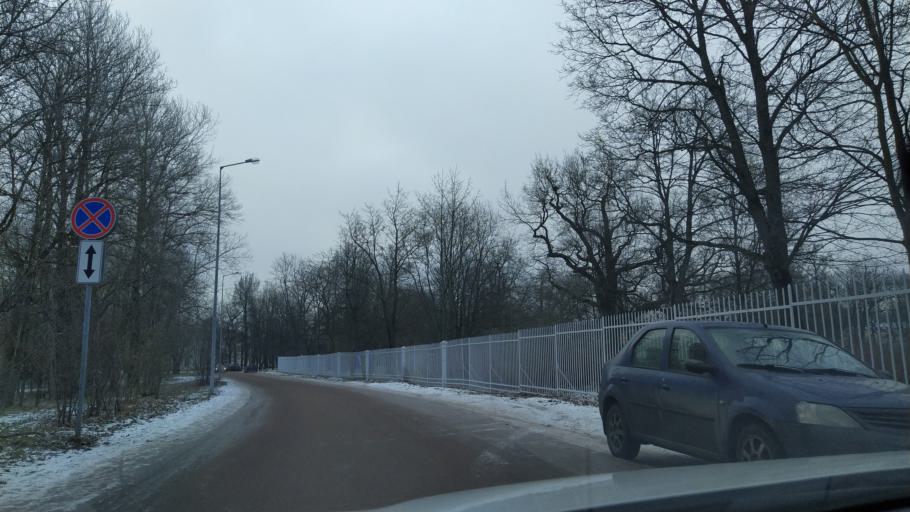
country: RU
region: St.-Petersburg
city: Pushkin
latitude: 59.7234
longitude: 30.3934
